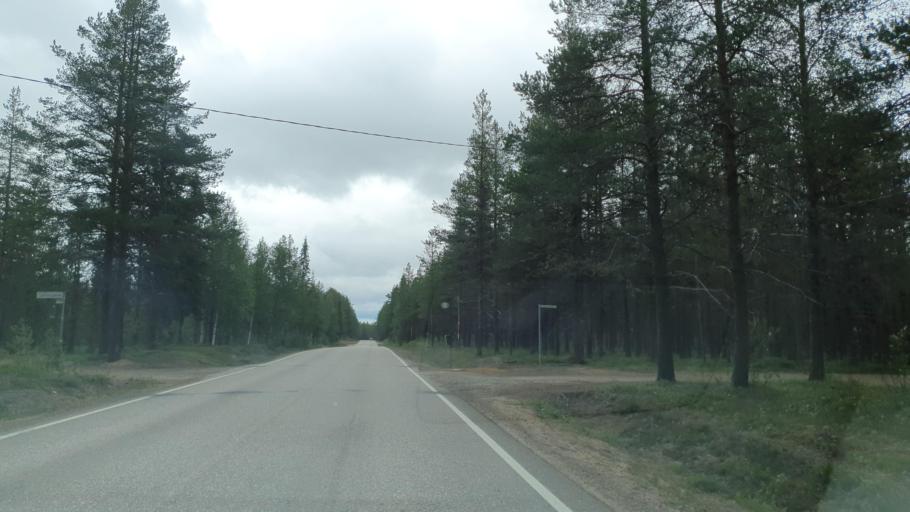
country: FI
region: Lapland
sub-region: Tunturi-Lappi
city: Kolari
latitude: 67.5478
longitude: 23.9794
